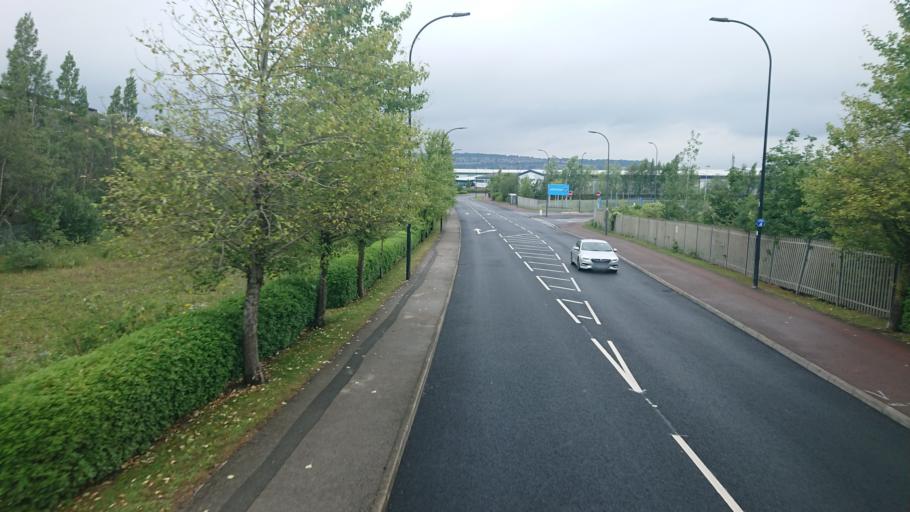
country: GB
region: England
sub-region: Rotherham
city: Orgreave
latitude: 53.3980
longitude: -1.4022
